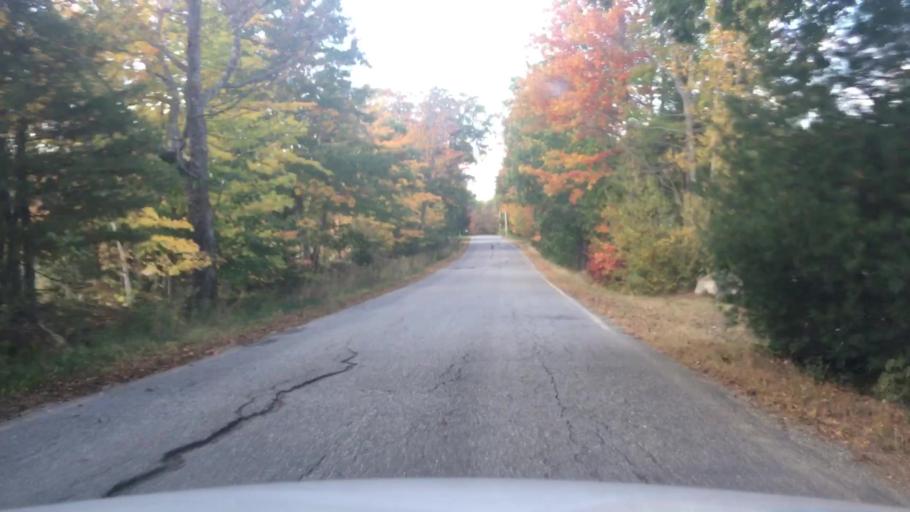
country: US
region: Maine
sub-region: Knox County
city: Washington
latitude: 44.3521
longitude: -69.3875
